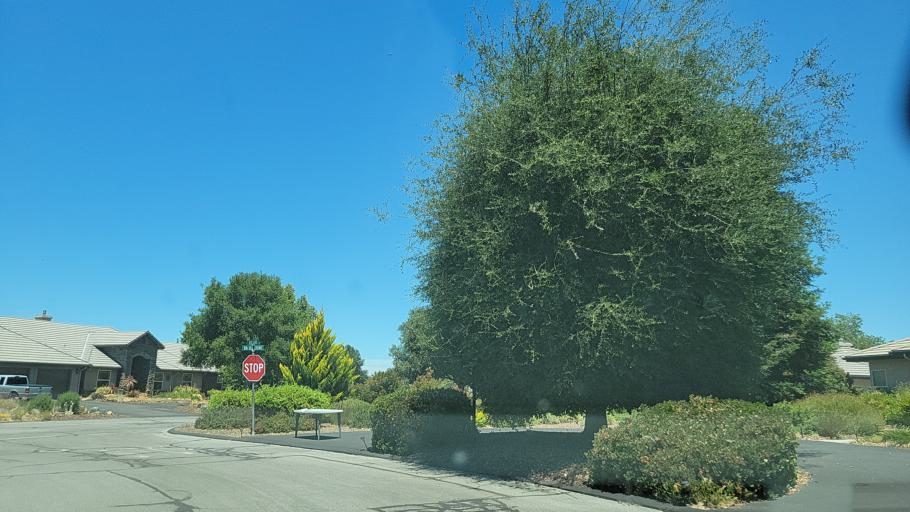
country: US
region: California
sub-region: San Luis Obispo County
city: Atascadero
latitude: 35.5104
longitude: -120.6657
